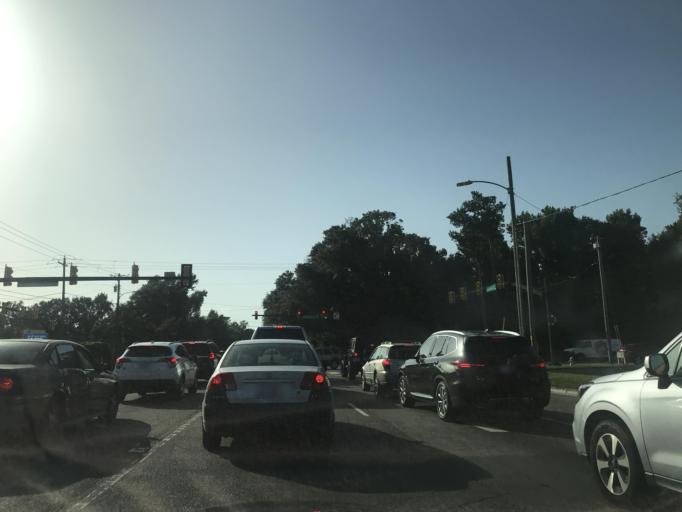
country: US
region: North Carolina
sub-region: New Hanover County
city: Wilmington
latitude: 34.2172
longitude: -77.9067
